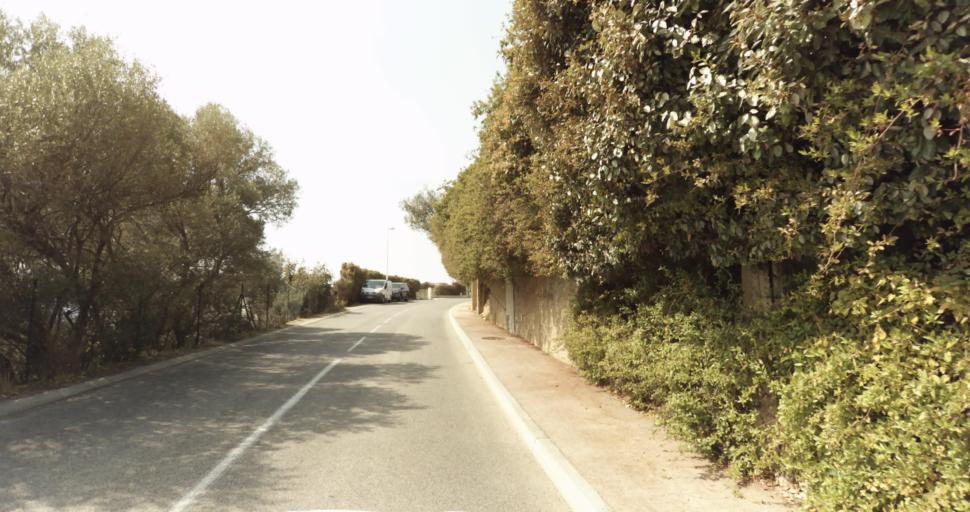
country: FR
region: Provence-Alpes-Cote d'Azur
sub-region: Departement du Var
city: Bormes-les-Mimosas
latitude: 43.1435
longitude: 6.3512
